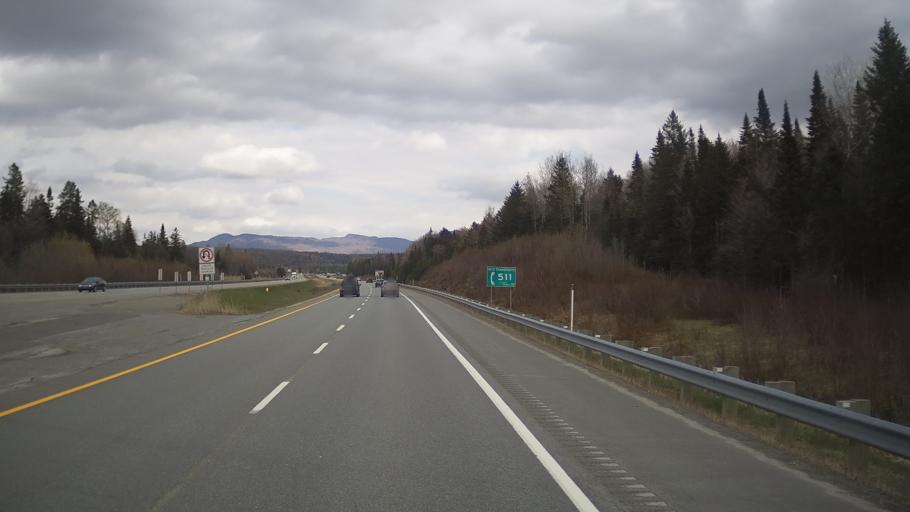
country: CA
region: Quebec
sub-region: Monteregie
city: Waterloo
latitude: 45.3024
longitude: -72.3700
